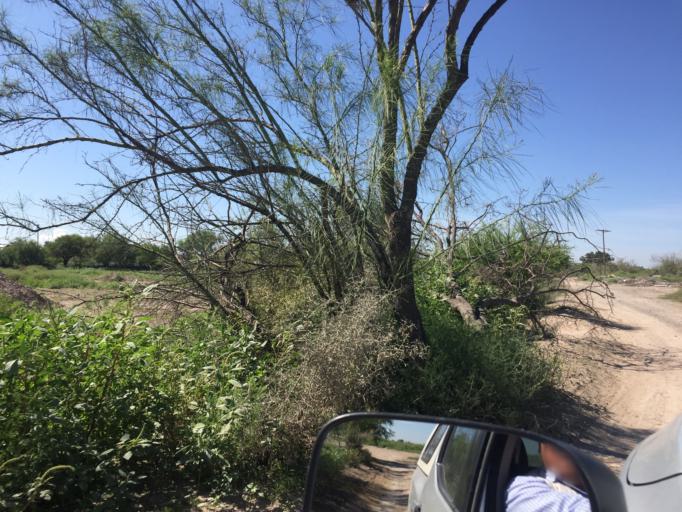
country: MX
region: Durango
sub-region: Gomez Palacio
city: San Felipe
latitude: 25.7244
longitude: -103.3754
